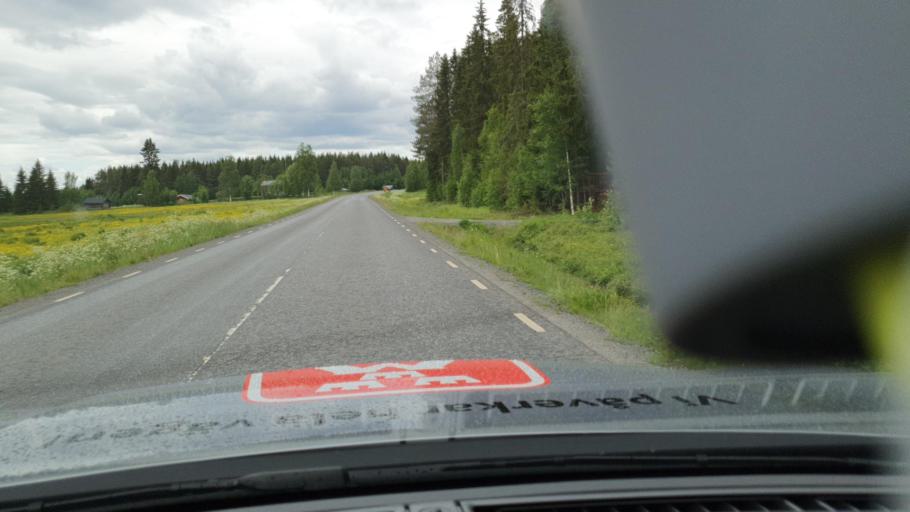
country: SE
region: Norrbotten
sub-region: Lulea Kommun
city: Ranea
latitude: 65.7833
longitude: 22.1662
